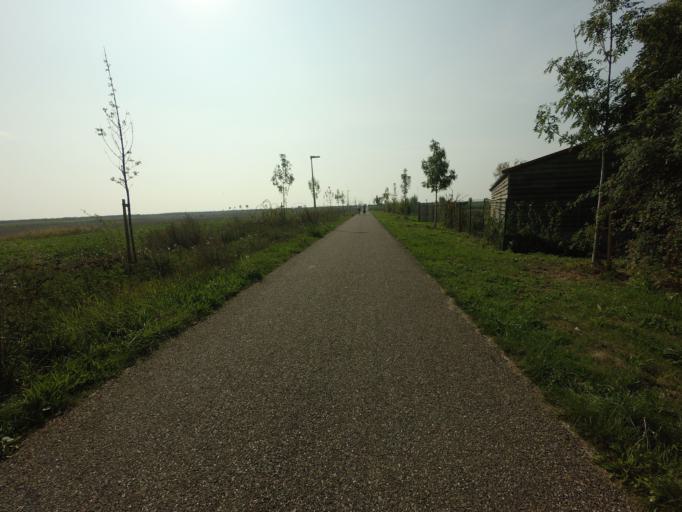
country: NL
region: Limburg
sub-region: Gemeente Maasgouw
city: Maasbracht
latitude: 51.1495
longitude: 5.8246
